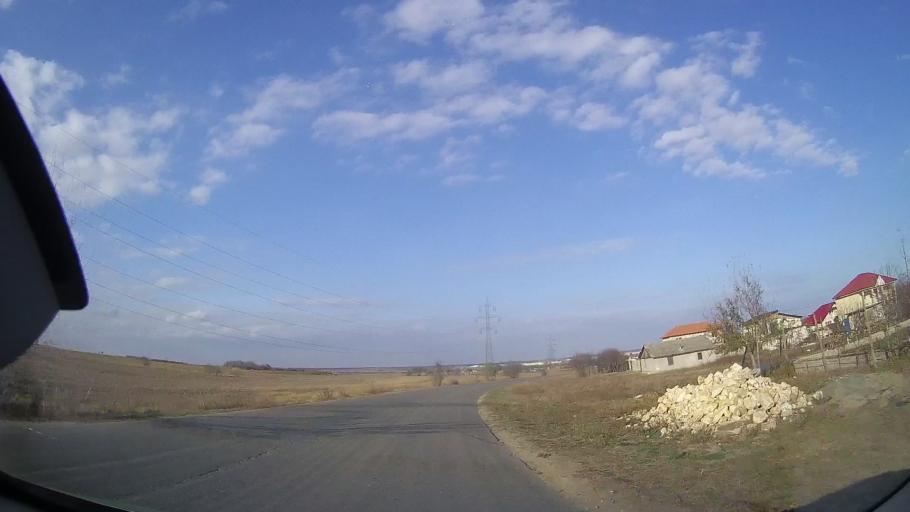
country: RO
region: Constanta
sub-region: Comuna Limanu
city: Limanu
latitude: 43.7958
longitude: 28.5202
